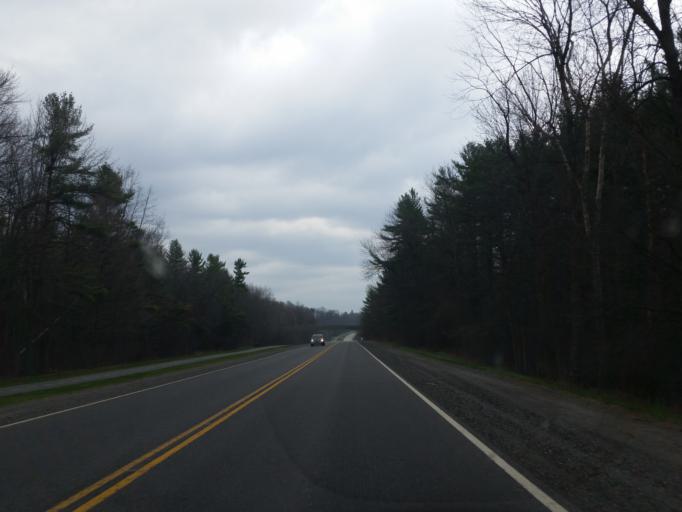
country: CA
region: Ontario
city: Brockville
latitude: 44.4988
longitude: -75.8097
